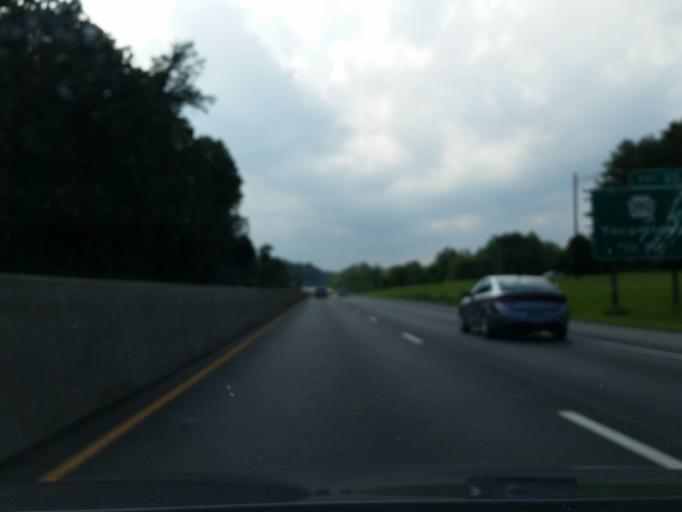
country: US
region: Pennsylvania
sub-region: York County
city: Valley Green
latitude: 40.1392
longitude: -76.8064
